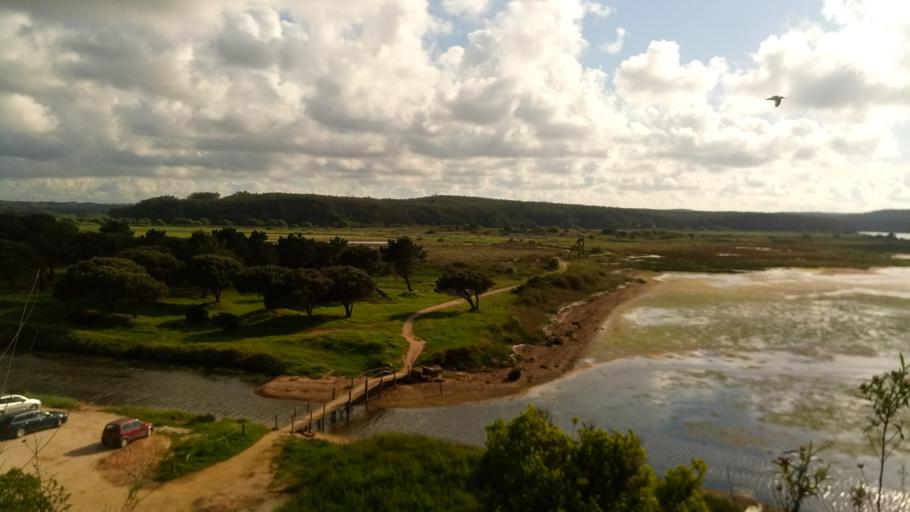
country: PT
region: Leiria
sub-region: Obidos
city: Obidos
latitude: 39.3996
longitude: -9.1976
